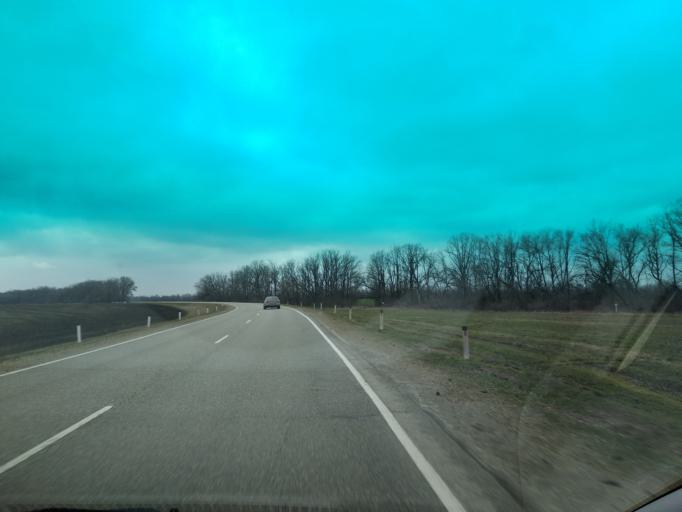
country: RU
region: Krasnodarskiy
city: Novorozhdestvenskaya
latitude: 45.7674
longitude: 39.9349
